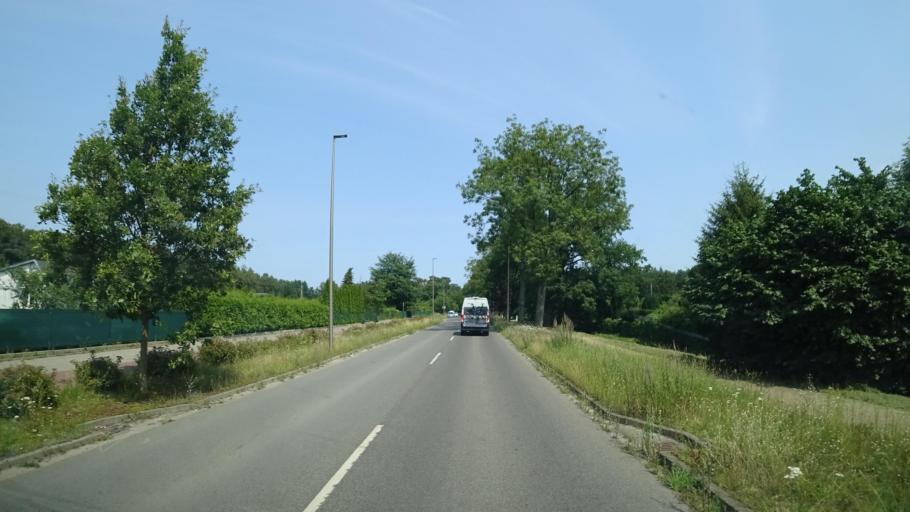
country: PL
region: West Pomeranian Voivodeship
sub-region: Swinoujscie
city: Swinoujscie
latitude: 53.8930
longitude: 14.2211
